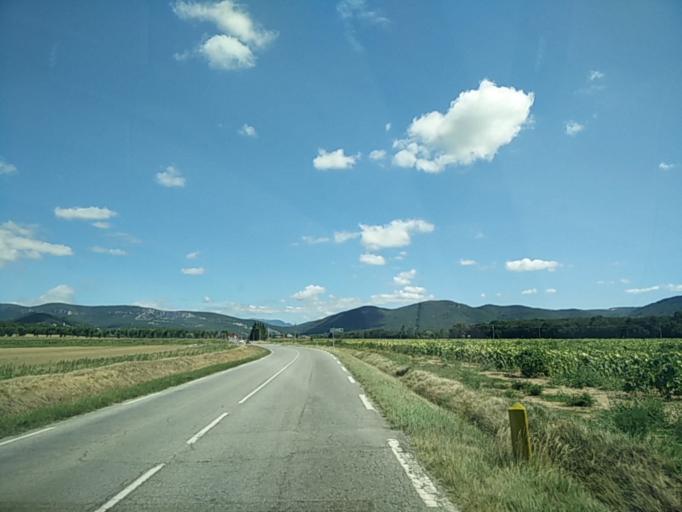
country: FR
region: Rhone-Alpes
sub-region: Departement de la Drome
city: La Begude-de-Mazenc
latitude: 44.5511
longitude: 4.9037
